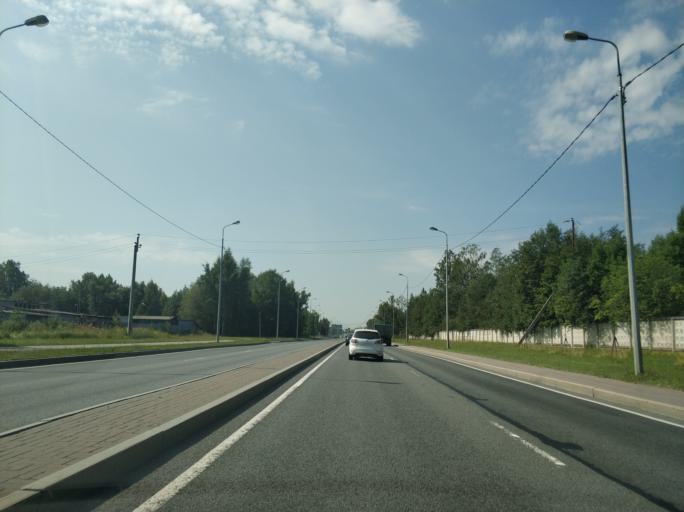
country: RU
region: St.-Petersburg
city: Krasnogvargeisky
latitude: 59.9896
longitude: 30.5277
